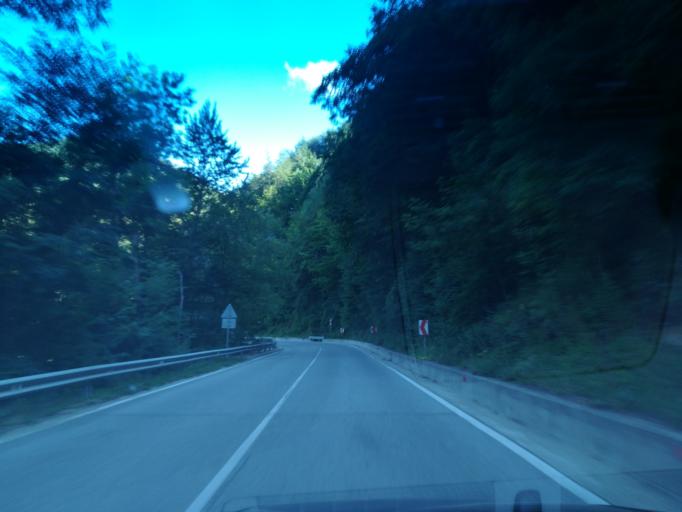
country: BG
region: Smolyan
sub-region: Obshtina Chepelare
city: Chepelare
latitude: 41.8052
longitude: 24.7087
